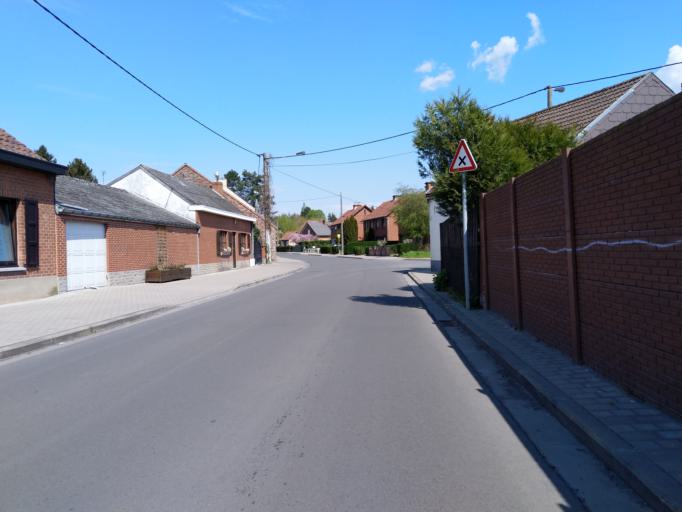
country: BE
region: Wallonia
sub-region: Province du Hainaut
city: Mons
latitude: 50.4736
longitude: 3.9222
